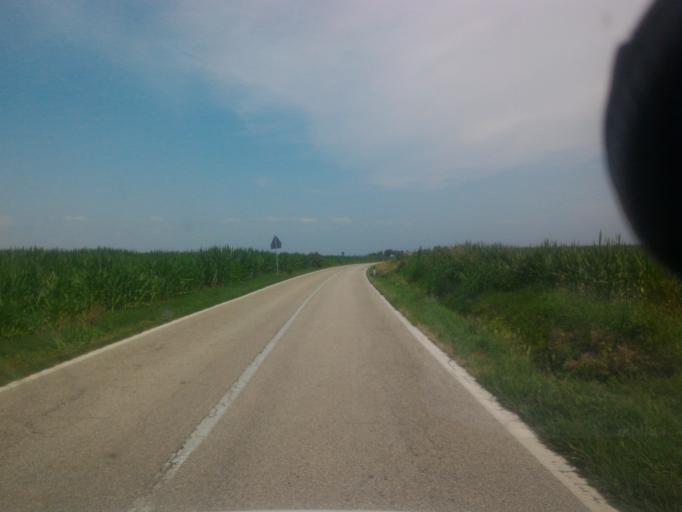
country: IT
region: Piedmont
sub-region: Provincia di Torino
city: Buriasco
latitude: 44.8601
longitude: 7.4257
